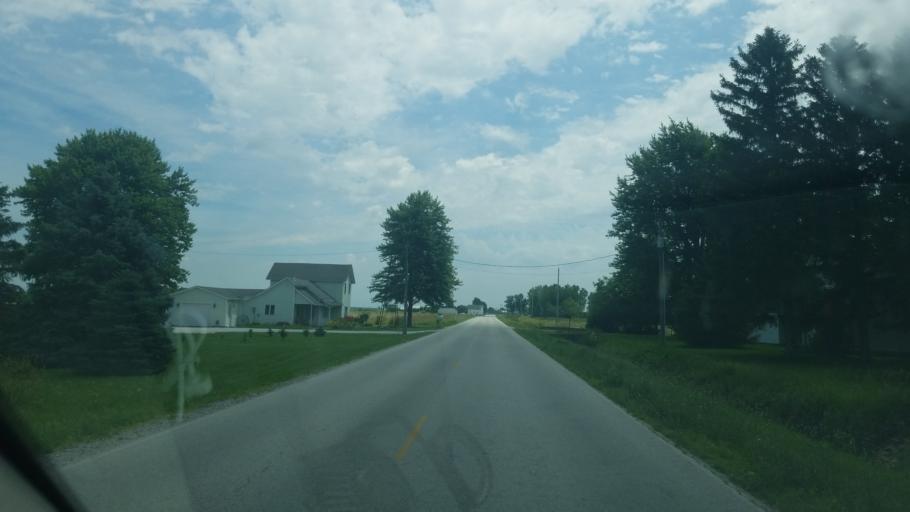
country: US
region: Ohio
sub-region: Wood County
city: Bowling Green
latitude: 41.2968
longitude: -83.6006
